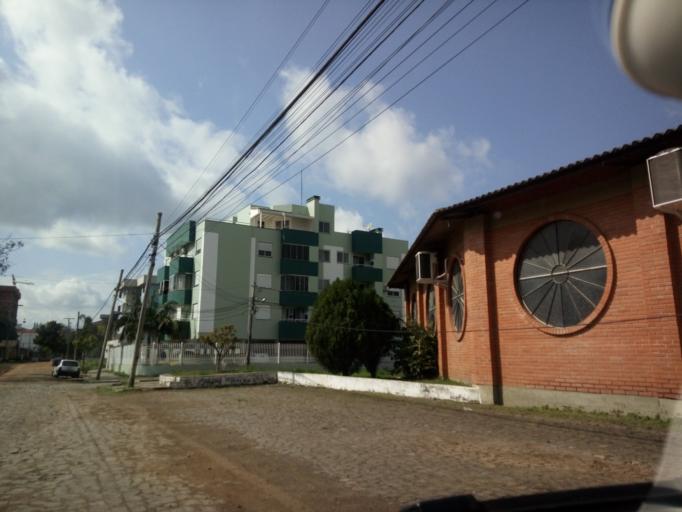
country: BR
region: Rio Grande do Sul
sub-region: Santa Maria
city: Santa Maria
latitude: -29.7028
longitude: -53.7219
